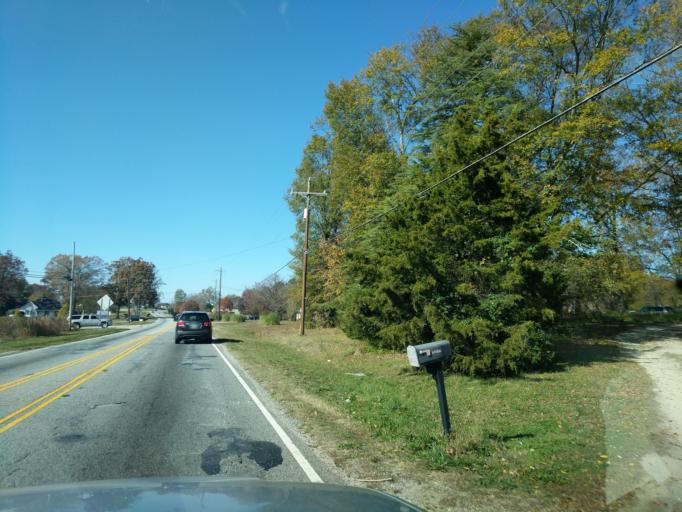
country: US
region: South Carolina
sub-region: Greenville County
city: Taylors
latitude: 34.9605
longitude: -82.3074
